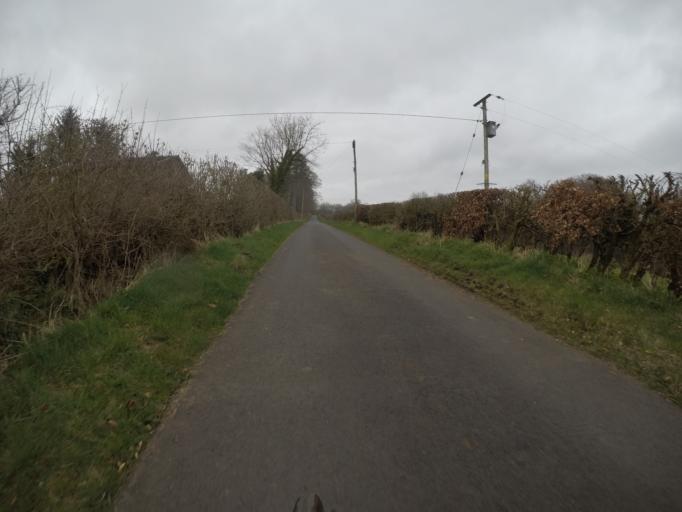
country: GB
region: Scotland
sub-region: East Ayrshire
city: Newmilns
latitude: 55.6151
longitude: -4.3537
